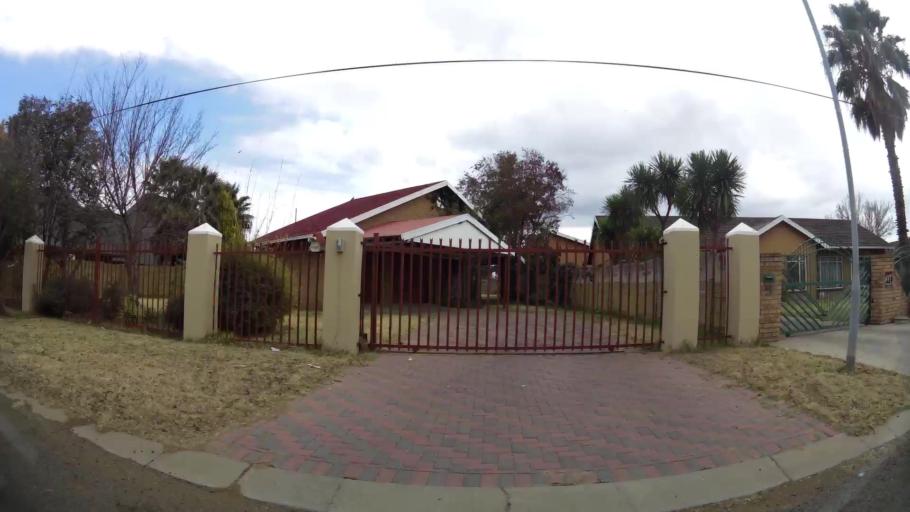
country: ZA
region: Orange Free State
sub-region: Fezile Dabi District Municipality
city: Kroonstad
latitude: -27.6294
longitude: 27.2400
